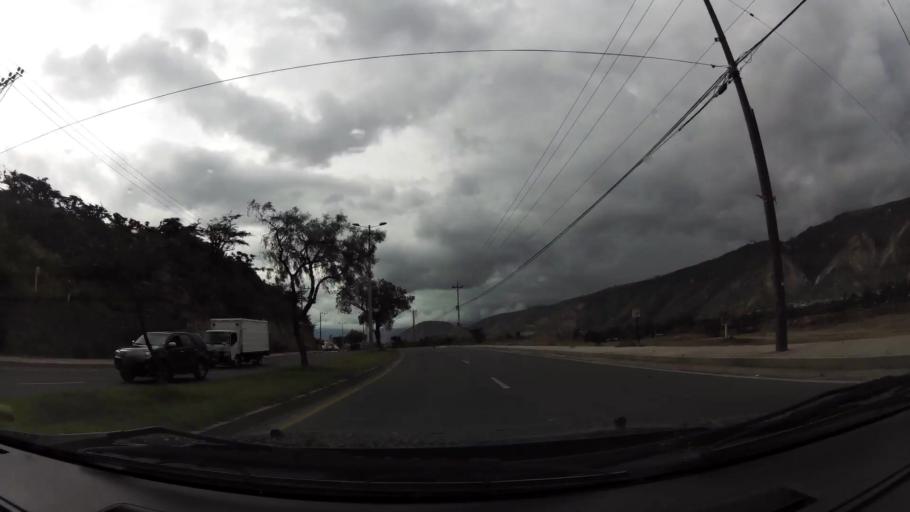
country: EC
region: Pichincha
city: Quito
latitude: -0.0393
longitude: -78.4543
